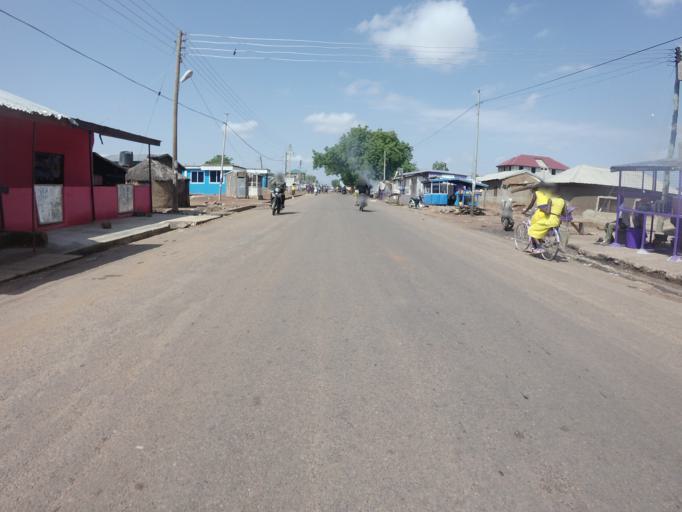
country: GH
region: Upper East
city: Bawku
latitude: 11.0615
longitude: -0.2355
